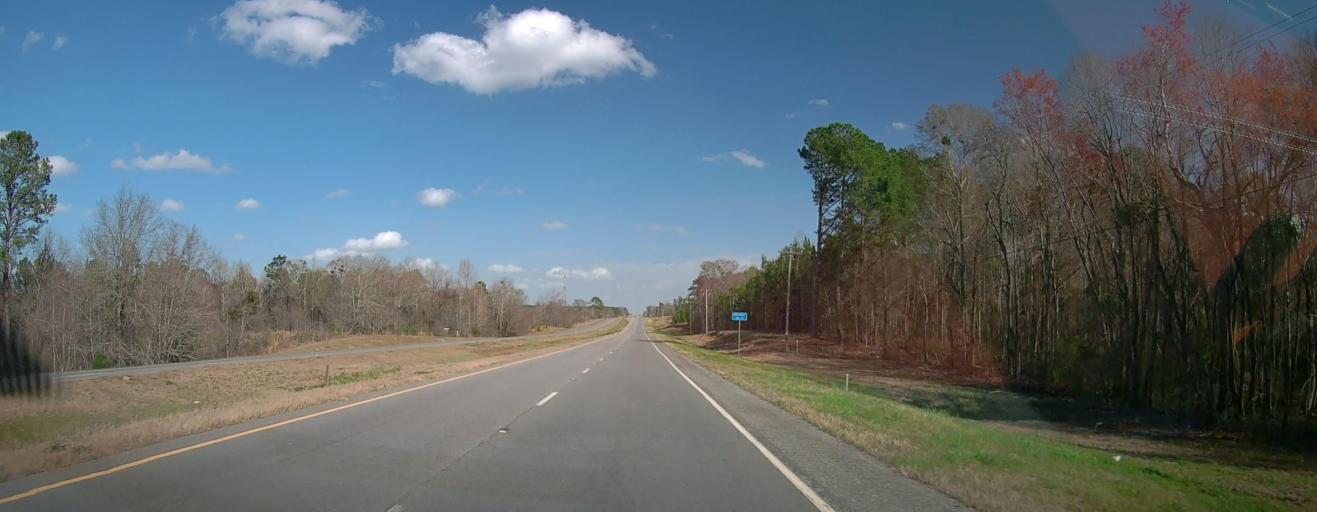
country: US
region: Georgia
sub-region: Dodge County
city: Eastman
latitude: 32.2036
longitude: -83.3067
